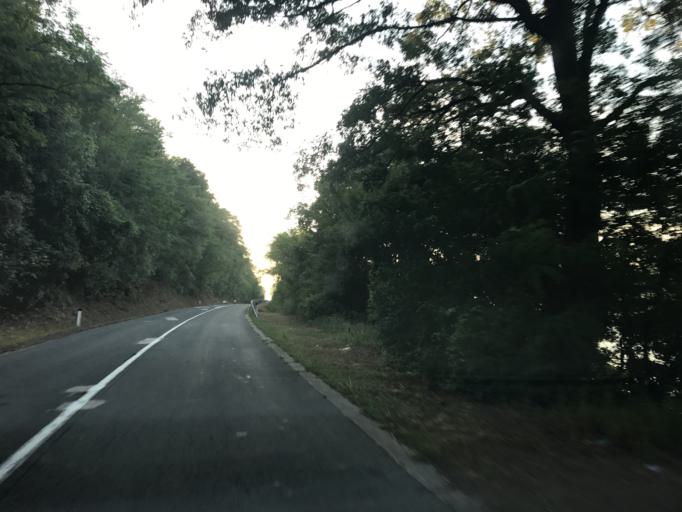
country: RO
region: Caras-Severin
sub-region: Comuna Berzasca
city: Berzasca
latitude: 44.6357
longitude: 21.9367
